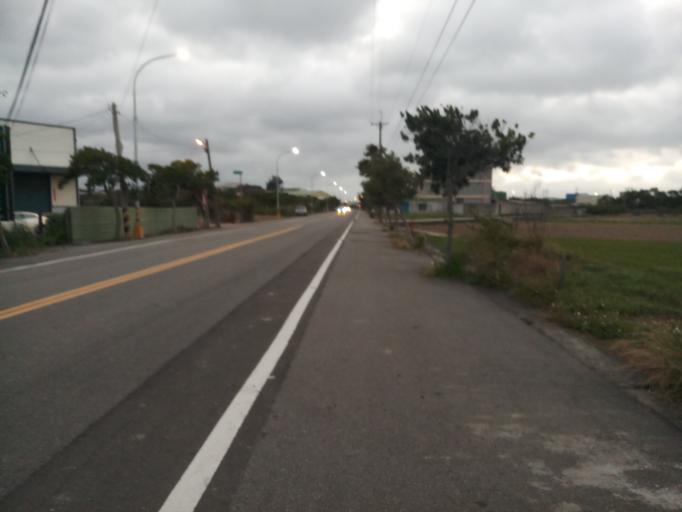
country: TW
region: Taiwan
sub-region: Miaoli
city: Miaoli
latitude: 24.6788
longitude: 120.8593
